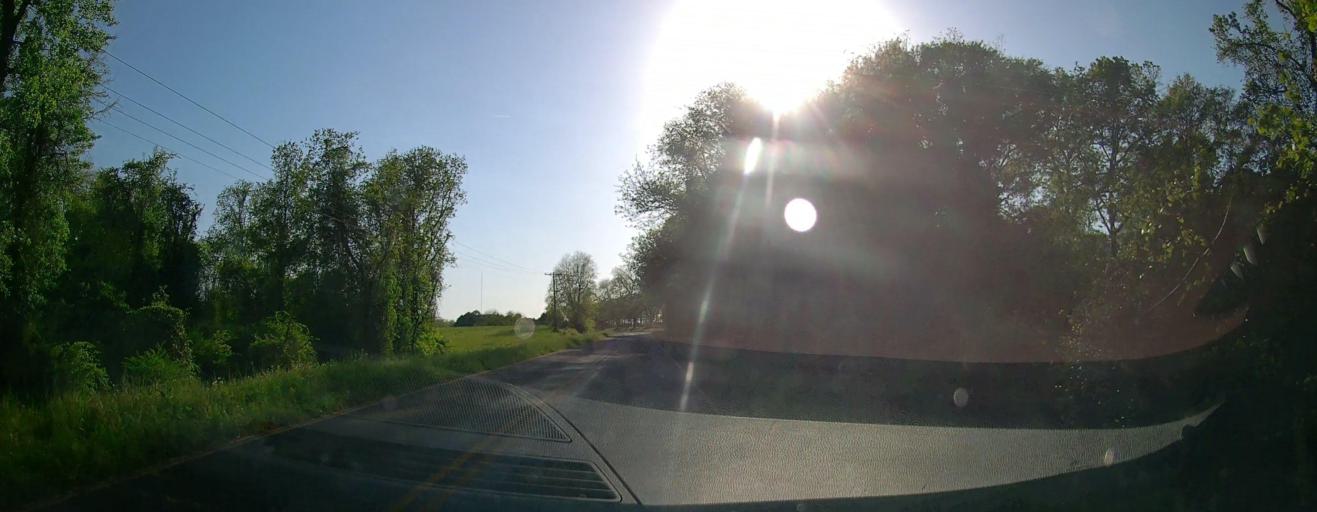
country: US
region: Georgia
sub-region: Macon County
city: Montezuma
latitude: 32.3361
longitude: -83.9512
